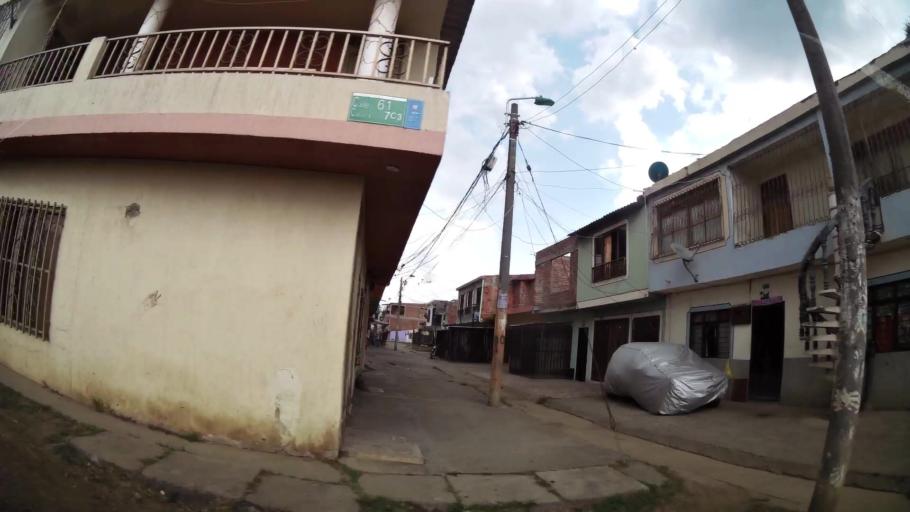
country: CO
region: Valle del Cauca
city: Cali
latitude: 3.4601
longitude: -76.4903
